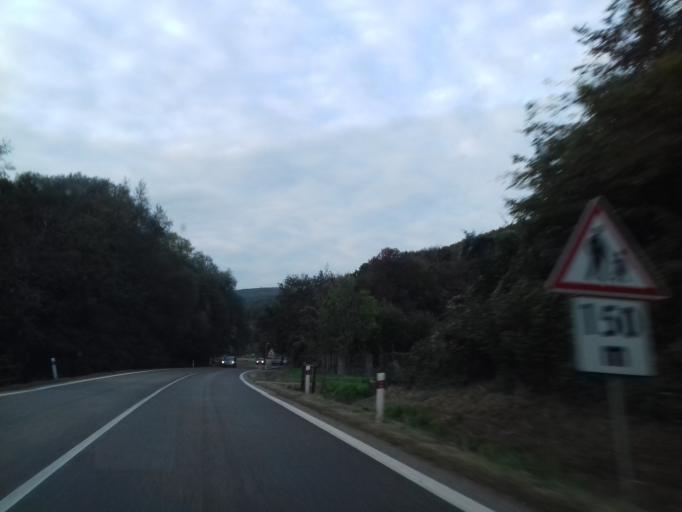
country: SK
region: Trenciansky
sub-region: Okres Trencin
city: Trencin
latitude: 48.9201
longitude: 17.9464
